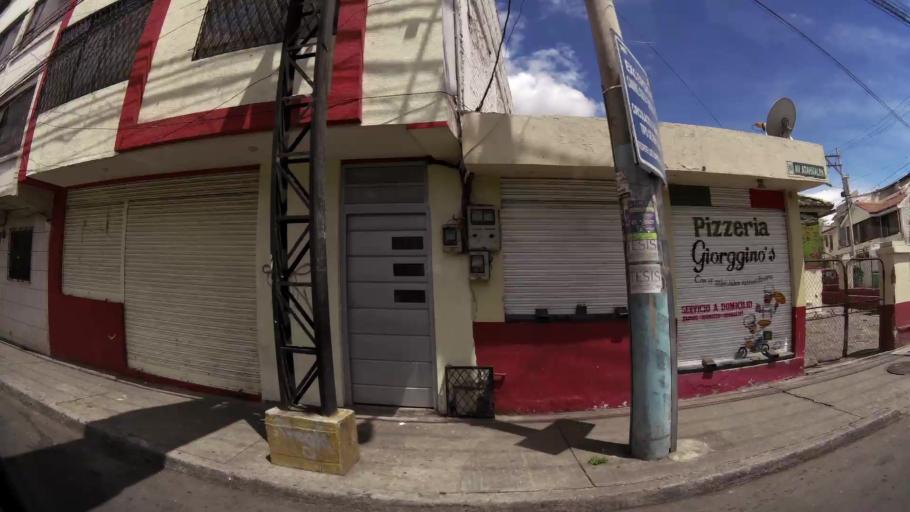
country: EC
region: Tungurahua
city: Ambato
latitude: -1.2492
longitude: -78.6322
